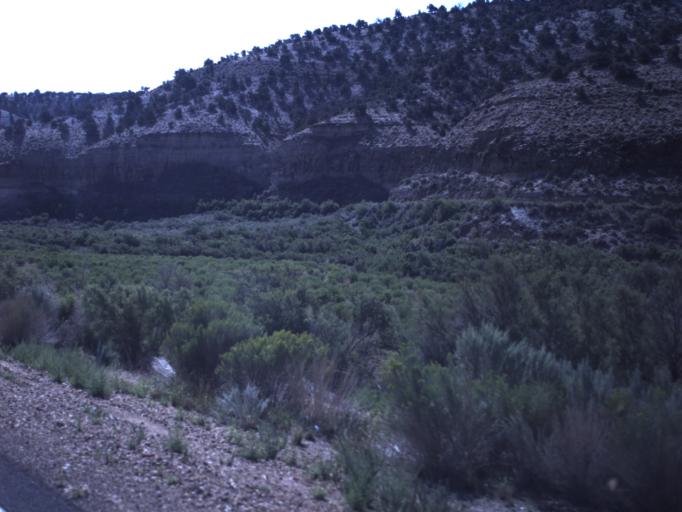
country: US
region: Utah
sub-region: Duchesne County
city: Duchesne
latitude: 40.1090
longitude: -110.4616
